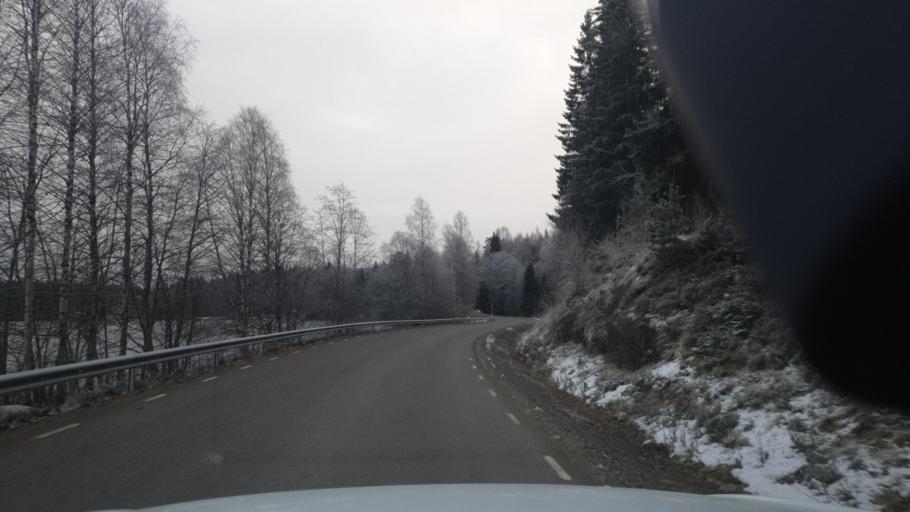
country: SE
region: Vaermland
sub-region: Eda Kommun
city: Charlottenberg
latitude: 60.0242
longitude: 12.6166
